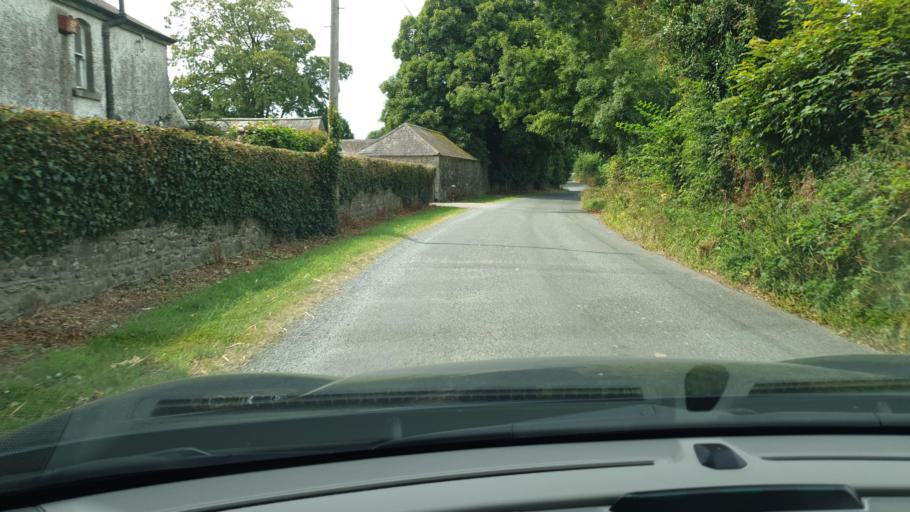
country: IE
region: Leinster
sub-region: An Mhi
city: Athboy
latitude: 53.6630
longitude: -6.9340
